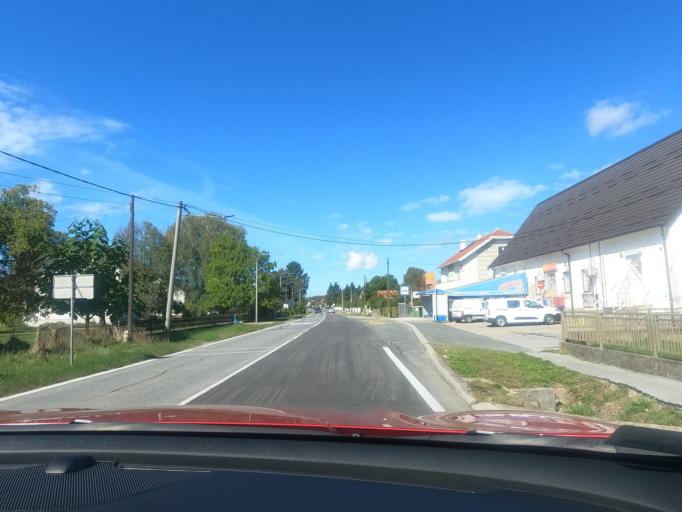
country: HR
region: Sisacko-Moslavacka
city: Lekenik
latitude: 45.6012
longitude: 16.1718
